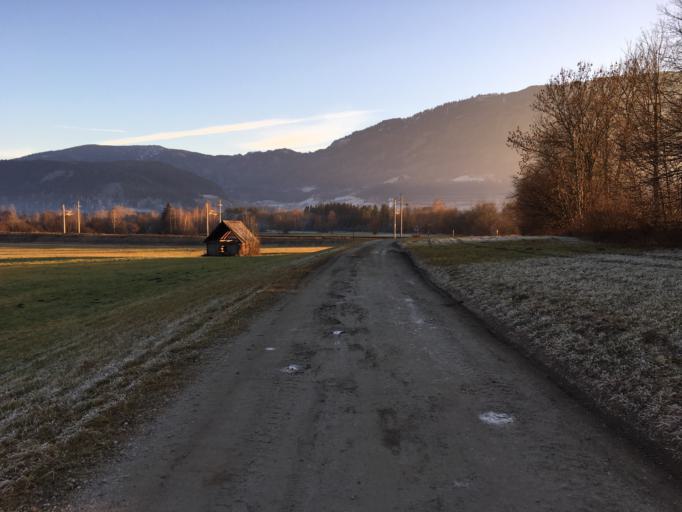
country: AT
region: Styria
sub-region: Politischer Bezirk Liezen
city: Weissenbach bei Liezen
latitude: 47.5647
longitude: 14.1962
